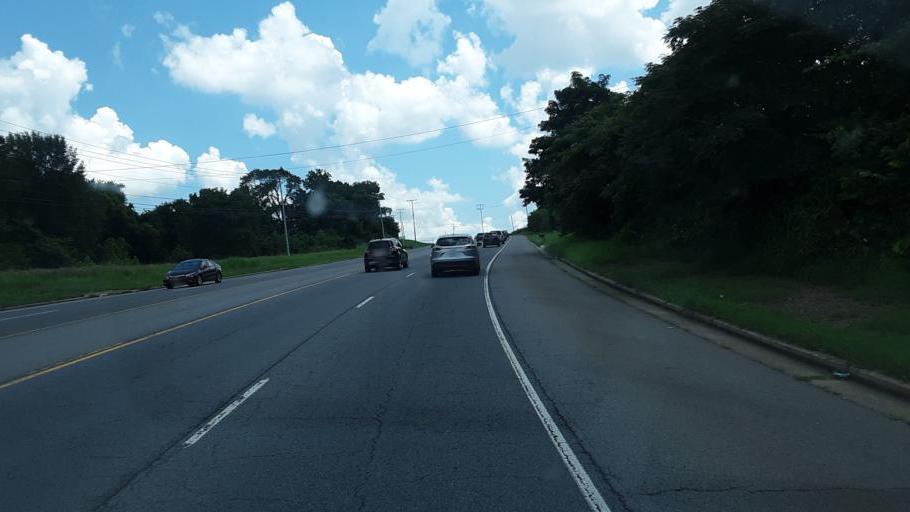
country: US
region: Kentucky
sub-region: Christian County
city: Oak Grove
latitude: 36.6263
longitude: -87.3638
